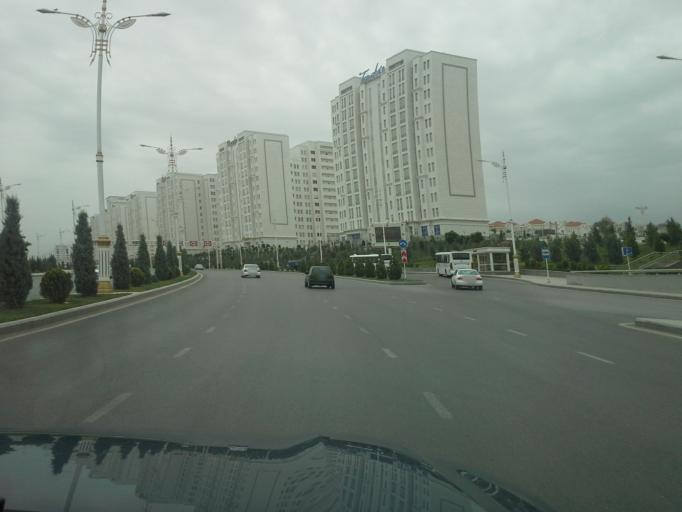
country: TM
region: Ahal
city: Ashgabat
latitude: 37.9392
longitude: 58.3645
